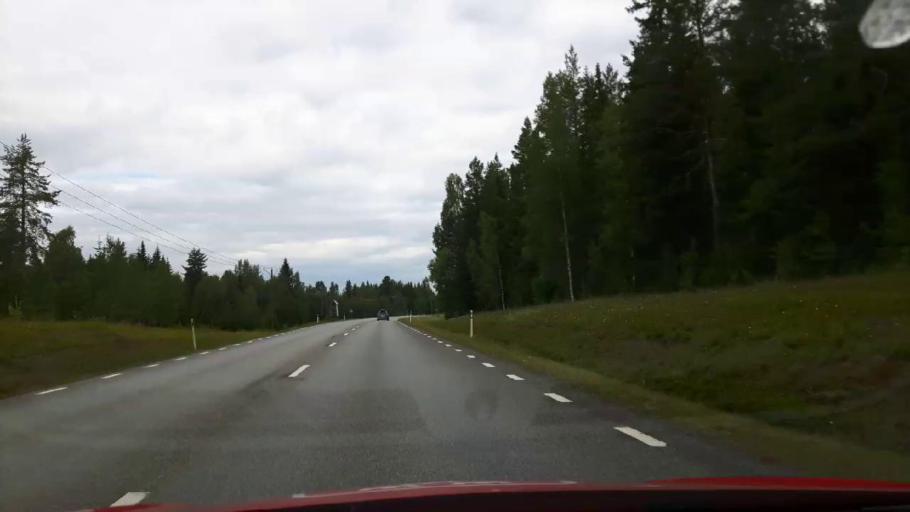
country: SE
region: Jaemtland
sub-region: Stroemsunds Kommun
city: Stroemsund
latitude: 63.6298
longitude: 15.3555
